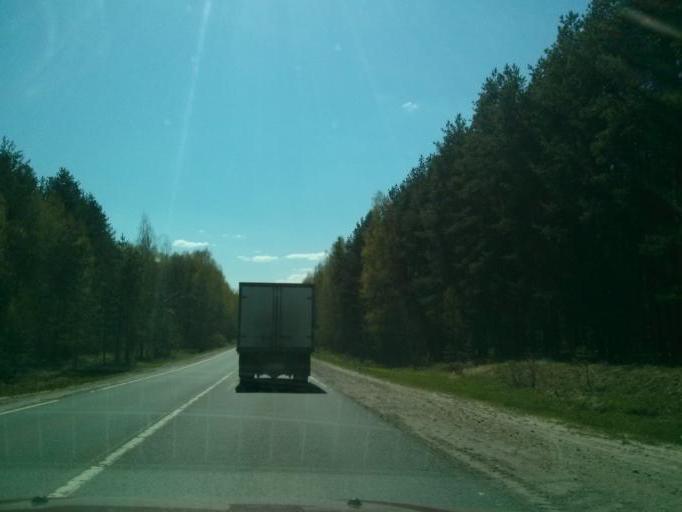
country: RU
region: Nizjnij Novgorod
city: Vorsma
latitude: 56.0220
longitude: 43.3528
